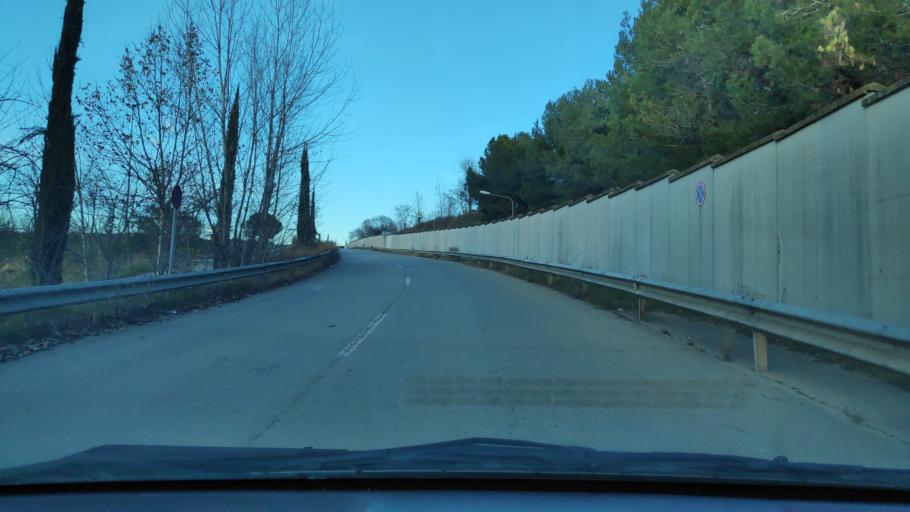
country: ES
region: Catalonia
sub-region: Provincia de Barcelona
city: Parets del Valles
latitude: 41.5698
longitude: 2.2542
